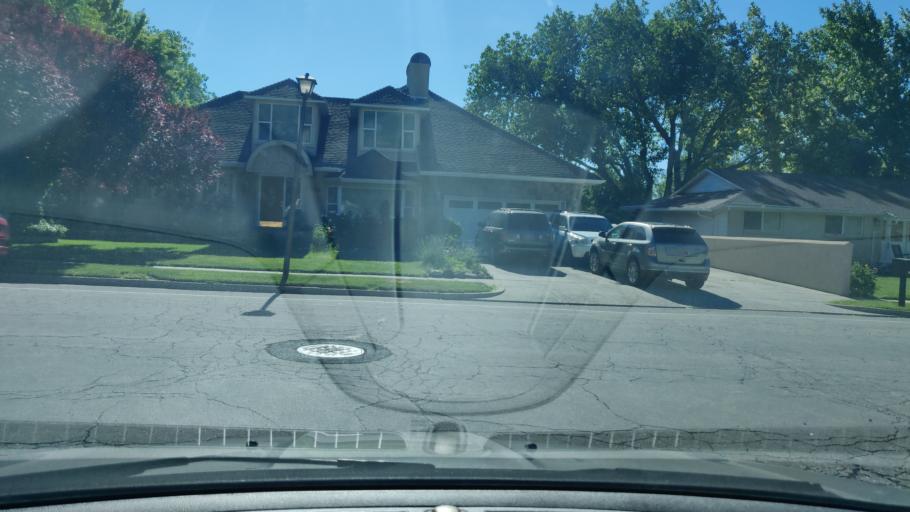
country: US
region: Utah
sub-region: Salt Lake County
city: Cottonwood Heights
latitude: 40.6100
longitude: -111.8076
